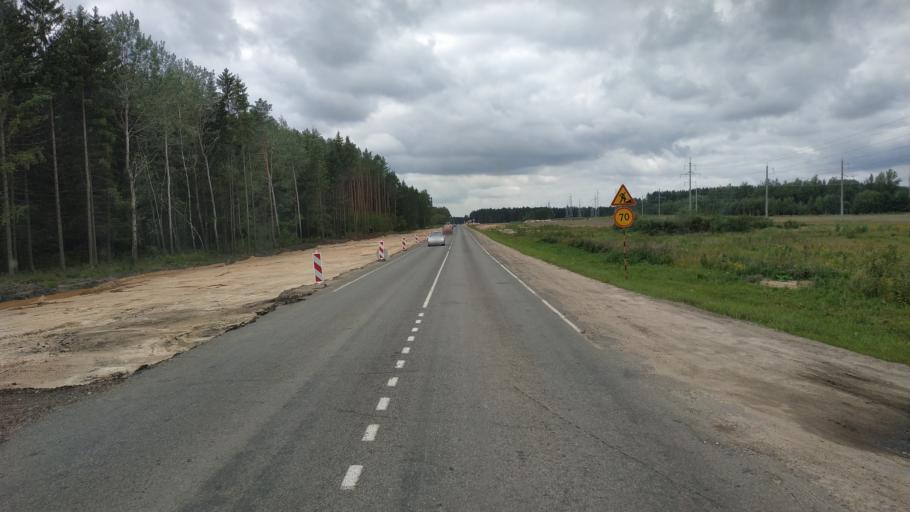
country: BY
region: Mogilev
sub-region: Mahilyowski Rayon
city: Veyno
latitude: 53.8737
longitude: 30.4410
